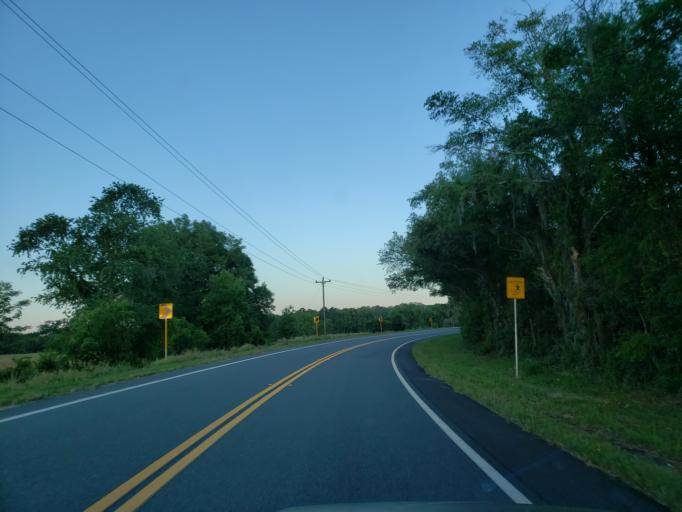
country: US
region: Georgia
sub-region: Echols County
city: Statenville
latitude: 30.5812
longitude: -83.1711
